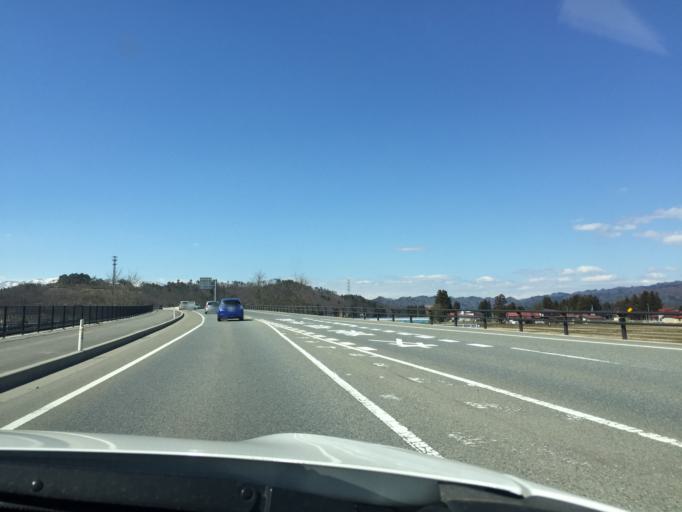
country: JP
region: Yamagata
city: Nagai
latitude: 38.0526
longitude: 140.0617
